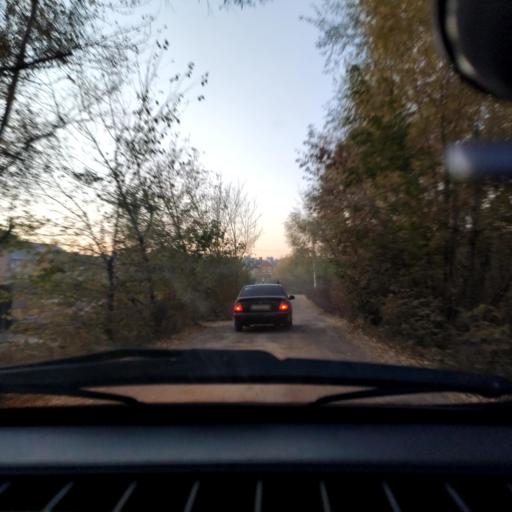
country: RU
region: Bashkortostan
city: Ufa
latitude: 54.6854
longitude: 55.9800
